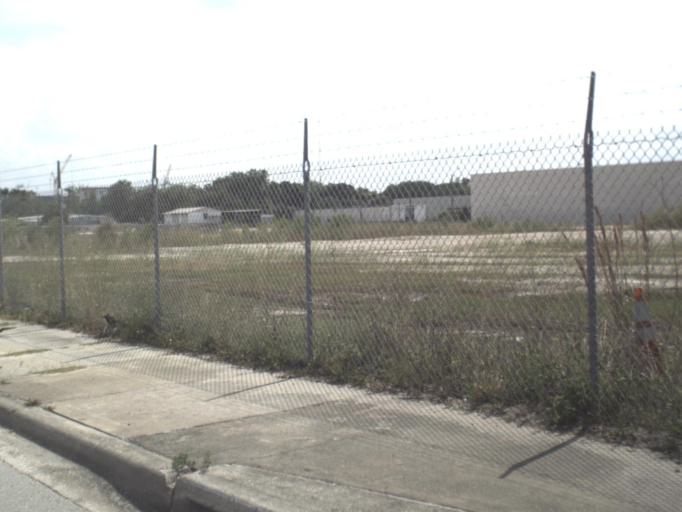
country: US
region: Florida
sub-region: Duval County
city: Jacksonville
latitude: 30.3337
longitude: -81.6312
